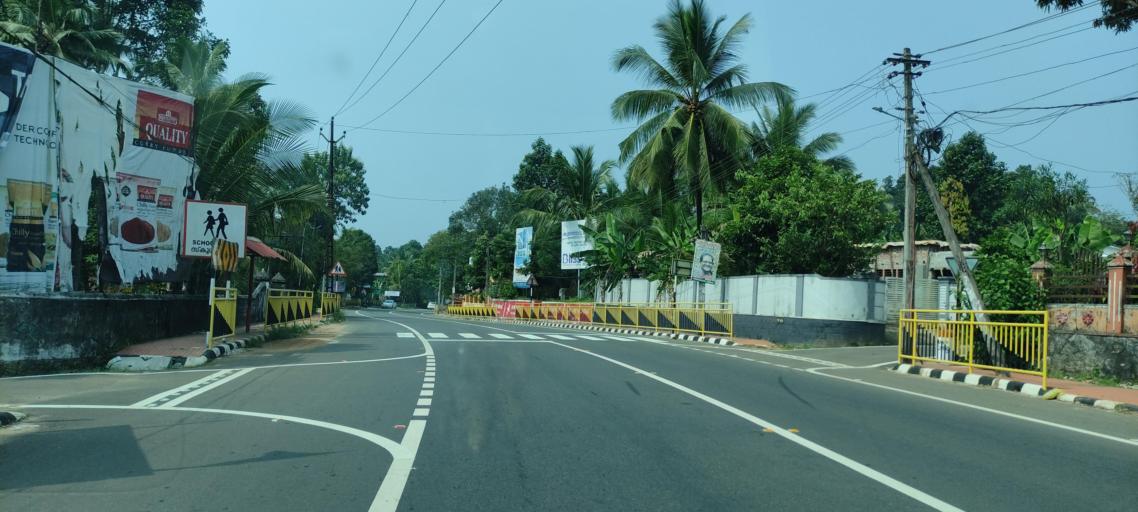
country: IN
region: Kerala
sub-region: Pattanamtitta
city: Adur
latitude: 9.2032
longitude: 76.6927
